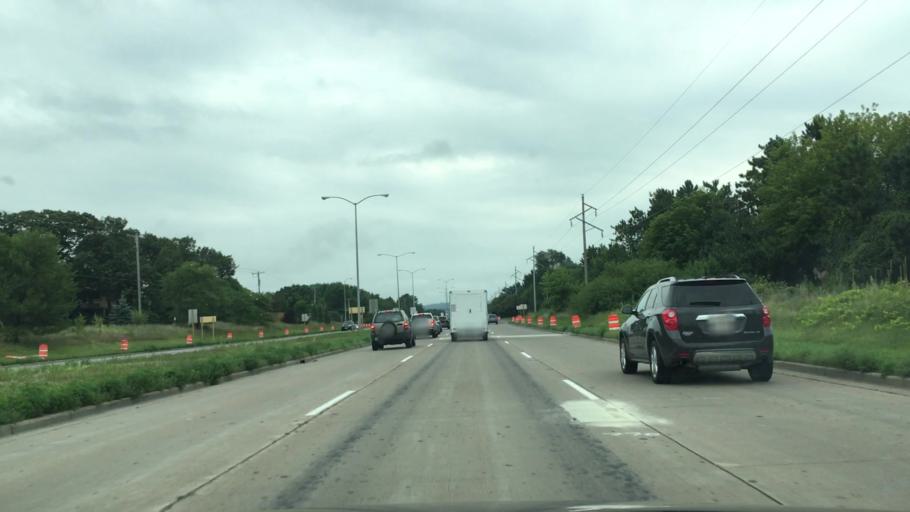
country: US
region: Wisconsin
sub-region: Eau Claire County
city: Eau Claire
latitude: 44.8123
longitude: -91.5385
